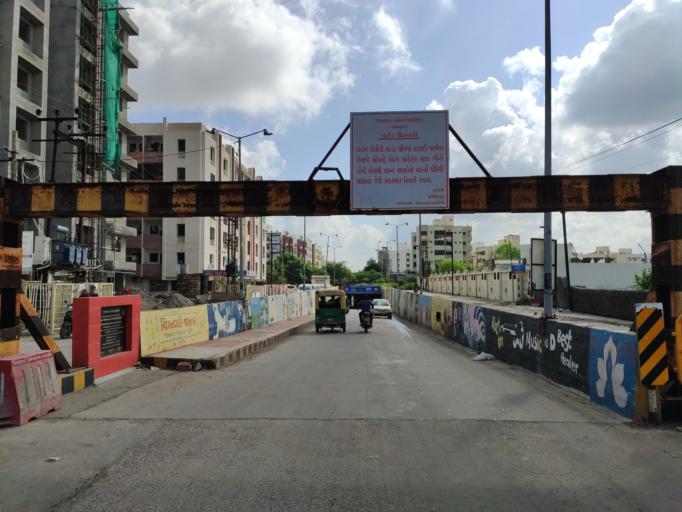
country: IN
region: Gujarat
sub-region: Jamnagar
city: Jamnagar
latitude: 22.4607
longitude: 70.0384
